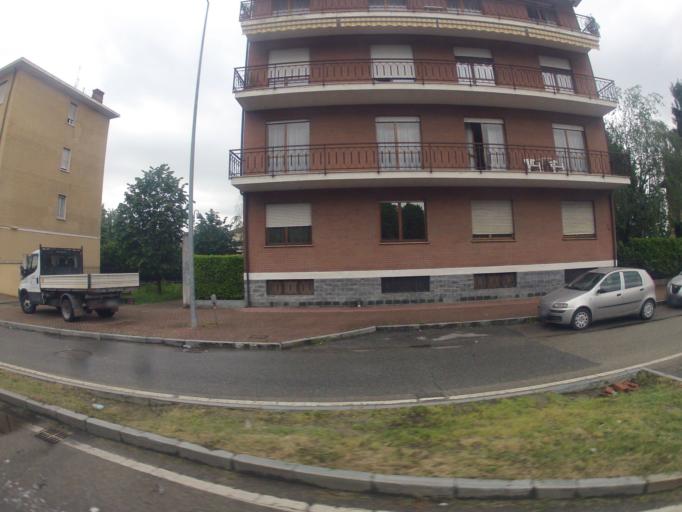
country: IT
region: Piedmont
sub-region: Provincia di Torino
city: Moncalieri
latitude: 44.9991
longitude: 7.6719
